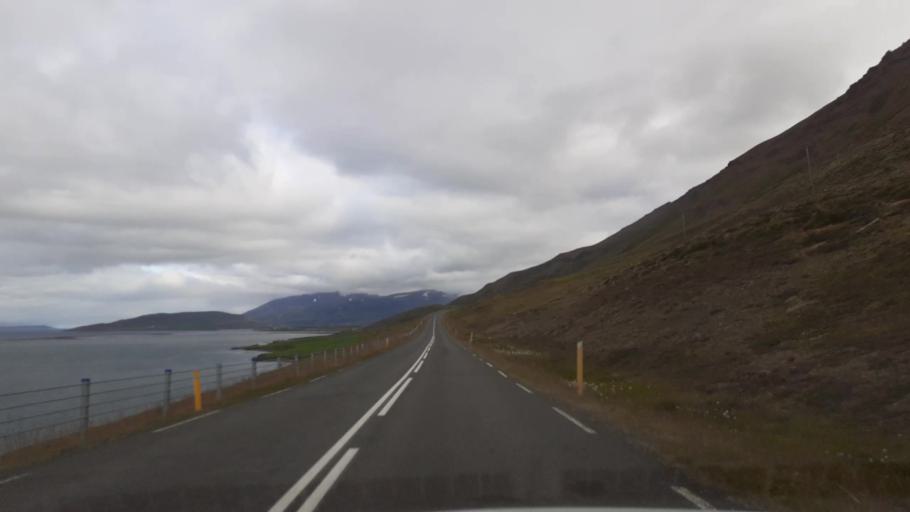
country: IS
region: Northeast
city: Akureyri
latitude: 65.8438
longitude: -18.0574
